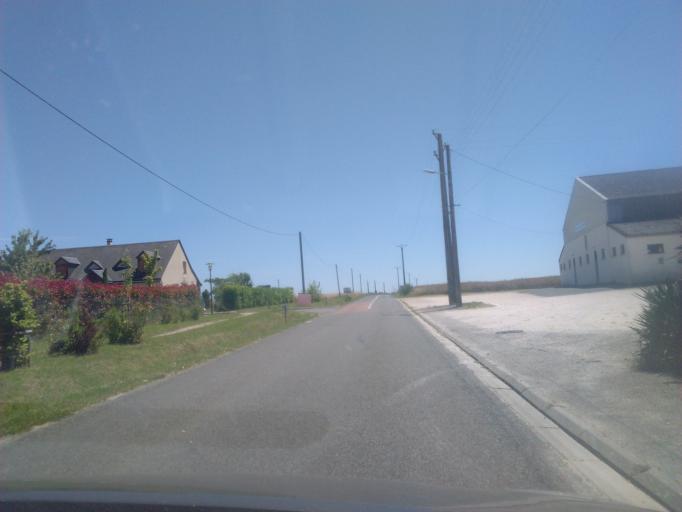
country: FR
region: Centre
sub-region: Departement du Loir-et-Cher
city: Herbault
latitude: 47.6491
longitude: 1.1863
